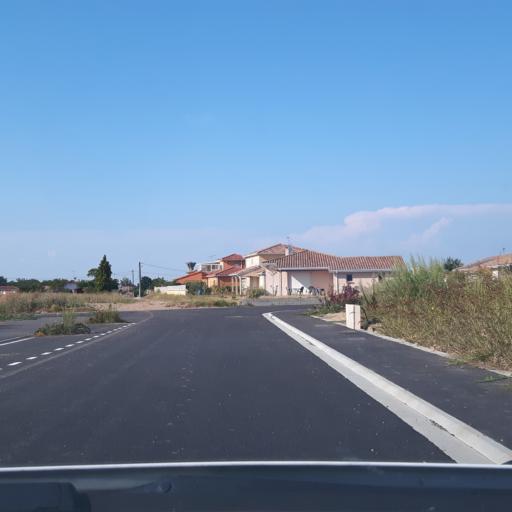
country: FR
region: Midi-Pyrenees
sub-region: Departement de la Haute-Garonne
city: Fronton
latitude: 43.8324
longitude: 1.3981
